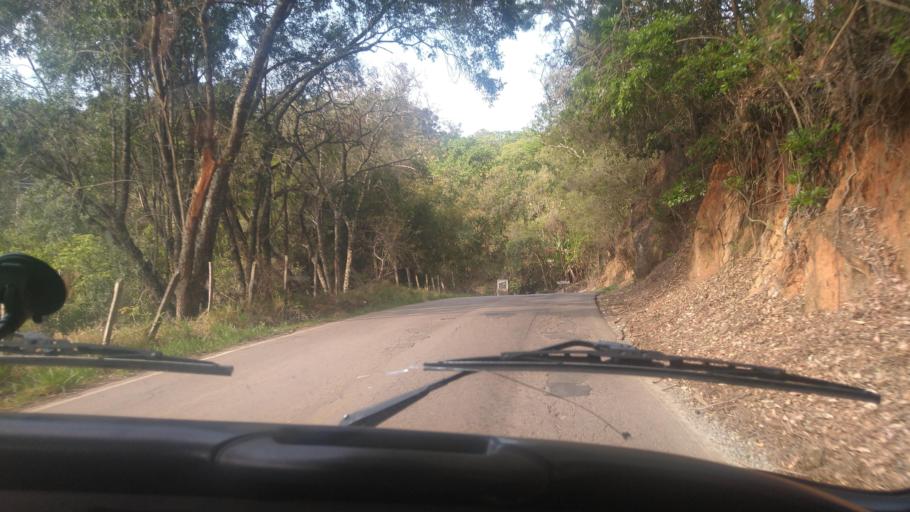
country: BR
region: Minas Gerais
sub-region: Extrema
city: Extrema
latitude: -22.7721
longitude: -46.4379
